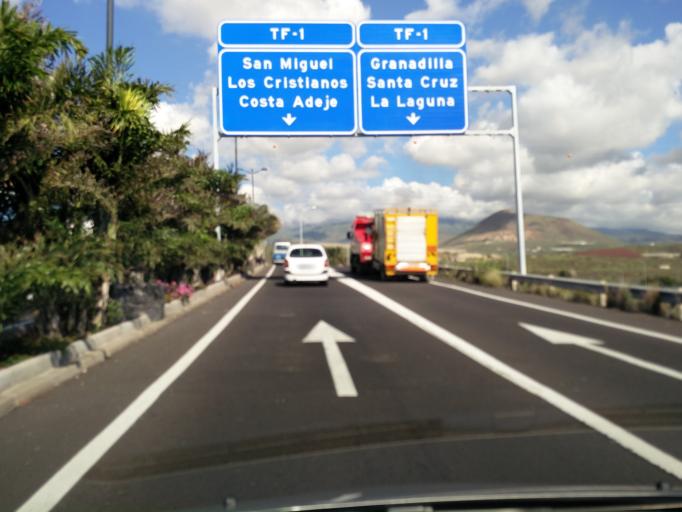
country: ES
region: Canary Islands
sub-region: Provincia de Santa Cruz de Tenerife
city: San Isidro
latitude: 28.0569
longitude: -16.5798
